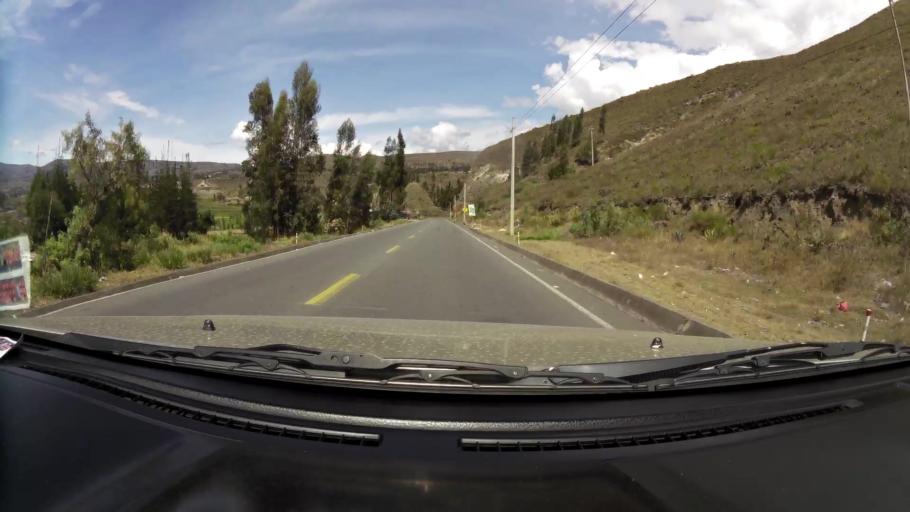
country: EC
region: Chimborazo
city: Guano
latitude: -1.6369
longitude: -78.5976
